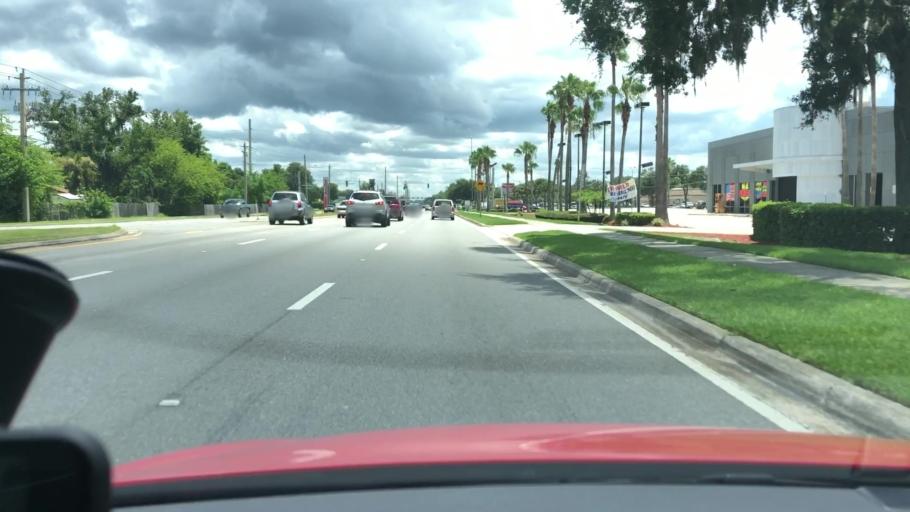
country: US
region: Florida
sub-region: Volusia County
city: Daytona Beach
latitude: 29.2086
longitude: -81.0427
